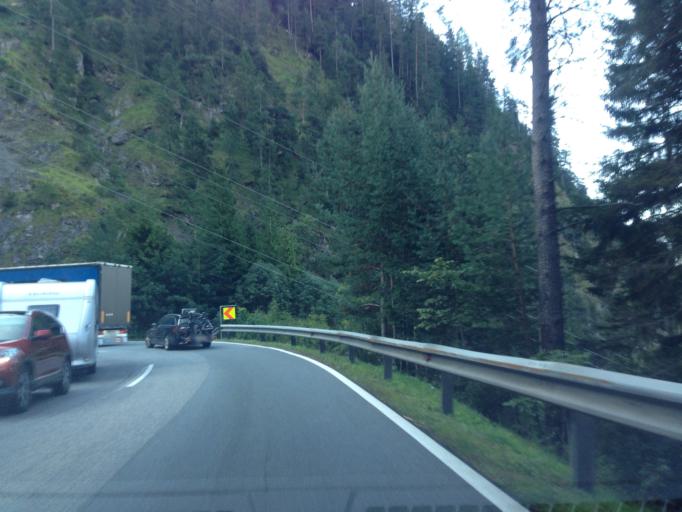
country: AT
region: Tyrol
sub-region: Politischer Bezirk Imst
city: Nassereith
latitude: 47.3526
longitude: 10.8414
